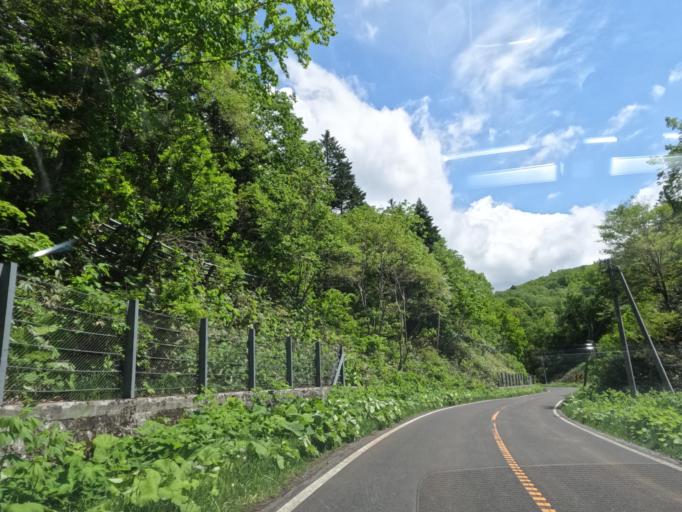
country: JP
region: Hokkaido
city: Takikawa
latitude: 43.5460
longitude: 141.6284
